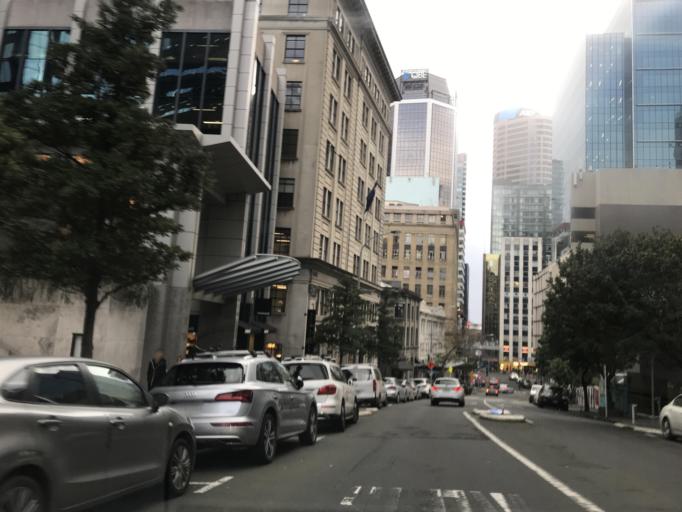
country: NZ
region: Auckland
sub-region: Auckland
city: Auckland
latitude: -36.8470
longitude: 174.7680
